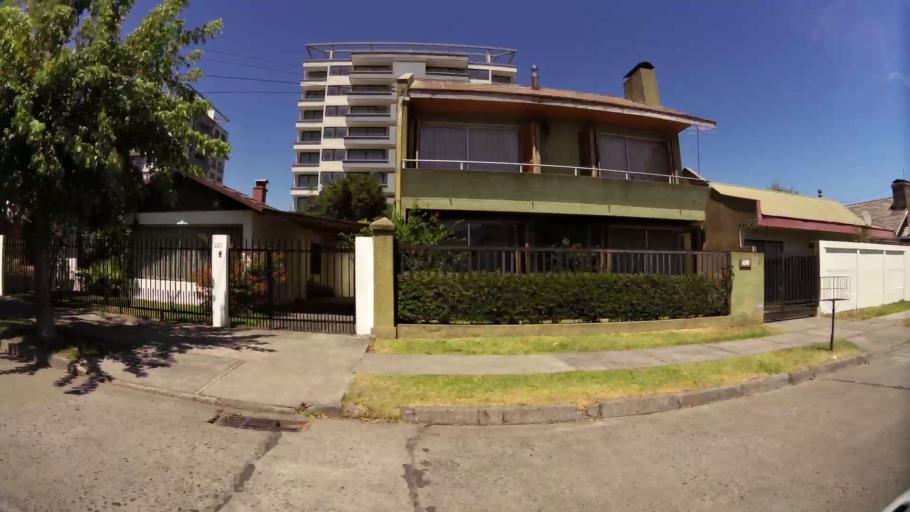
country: CL
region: Maule
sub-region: Provincia de Curico
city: Curico
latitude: -34.9881
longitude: -71.2298
